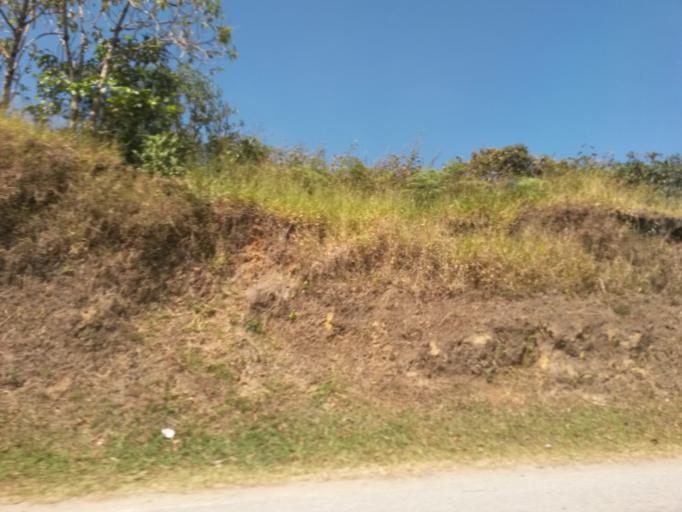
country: CO
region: Cauca
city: Popayan
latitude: 2.4570
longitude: -76.6477
